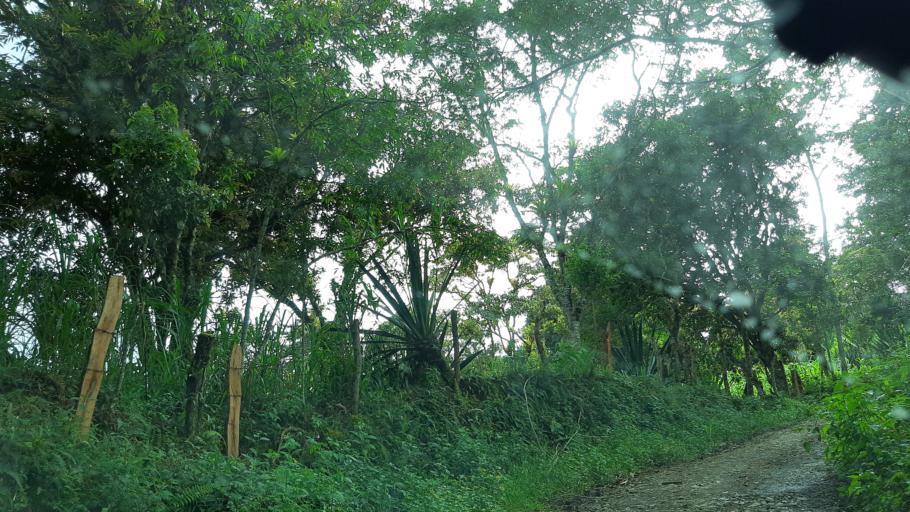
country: CO
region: Boyaca
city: Garagoa
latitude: 5.0419
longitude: -73.3462
